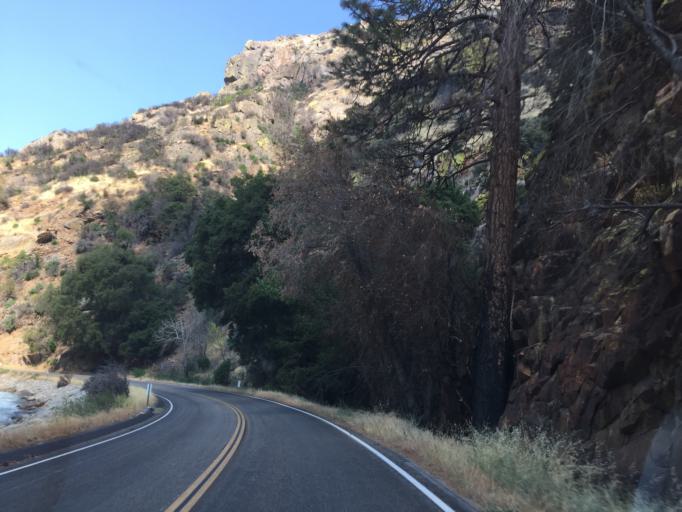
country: US
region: California
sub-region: Tulare County
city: Three Rivers
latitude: 36.8097
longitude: -118.7903
